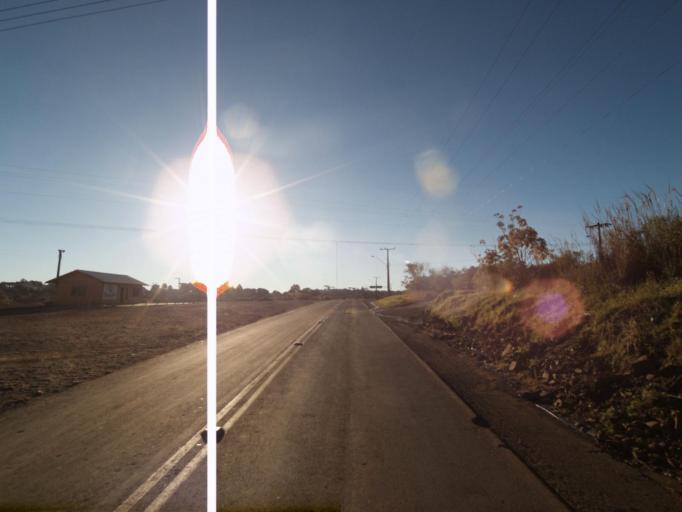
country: AR
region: Misiones
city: Bernardo de Irigoyen
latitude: -26.2660
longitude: -53.6386
